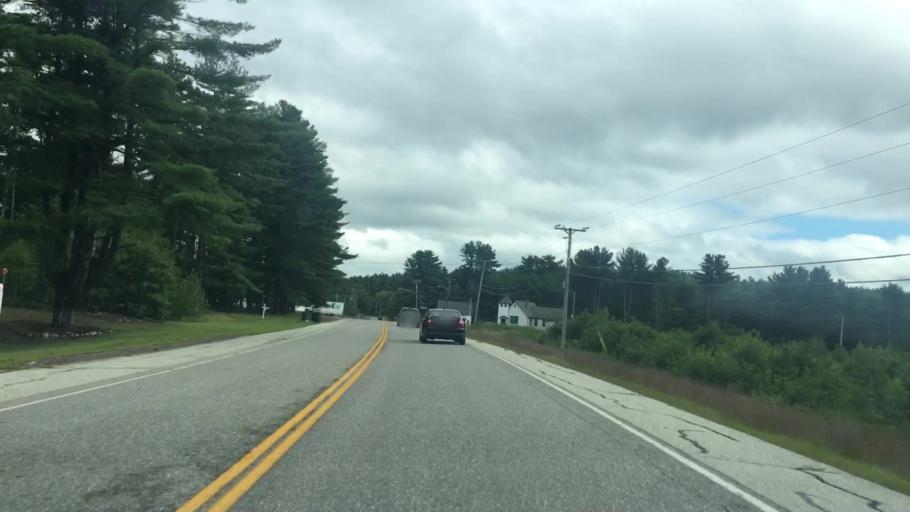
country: US
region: Maine
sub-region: York County
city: Lake Arrowhead
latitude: 43.6218
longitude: -70.7370
